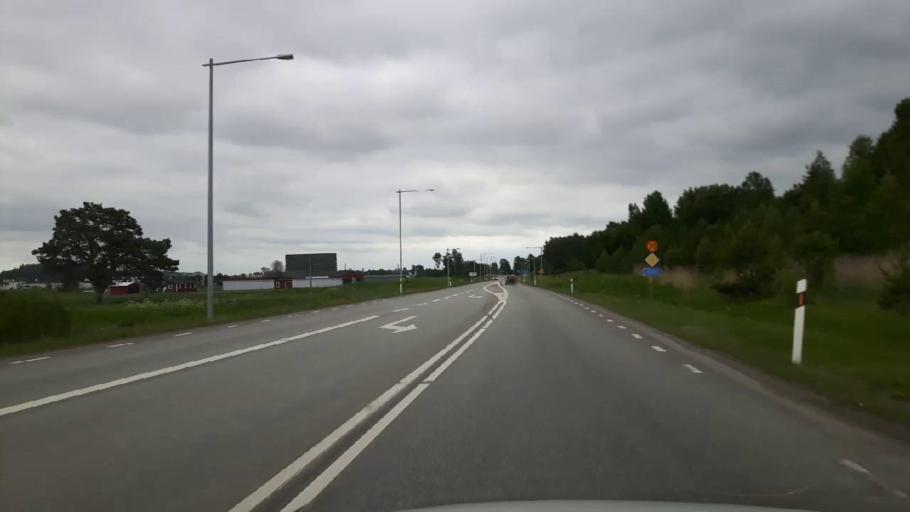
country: SE
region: Vaestmanland
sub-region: Kopings Kommun
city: Koping
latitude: 59.5275
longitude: 15.9605
